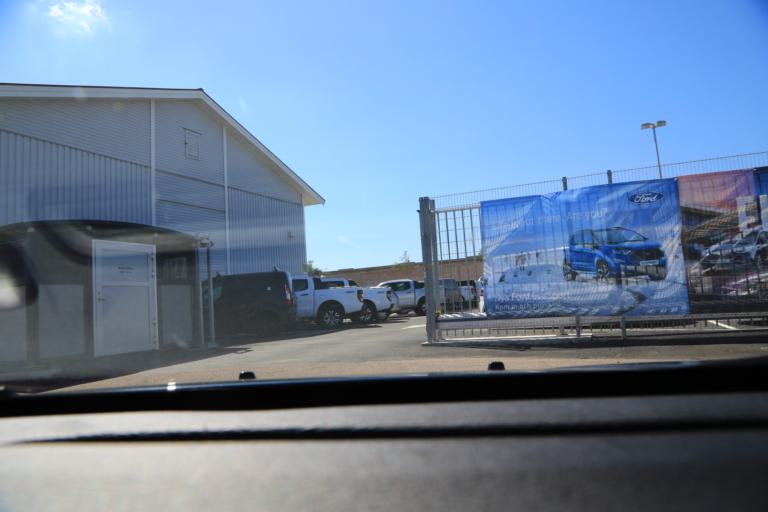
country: SE
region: Halland
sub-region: Kungsbacka Kommun
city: Kungsbacka
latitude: 57.5115
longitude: 12.0756
